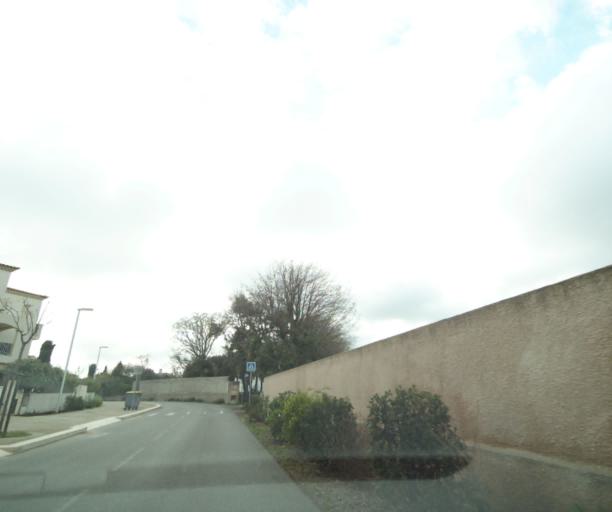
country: FR
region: Languedoc-Roussillon
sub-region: Departement de l'Herault
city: Saint-Jean-de-Vedas
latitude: 43.5823
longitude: 3.8244
